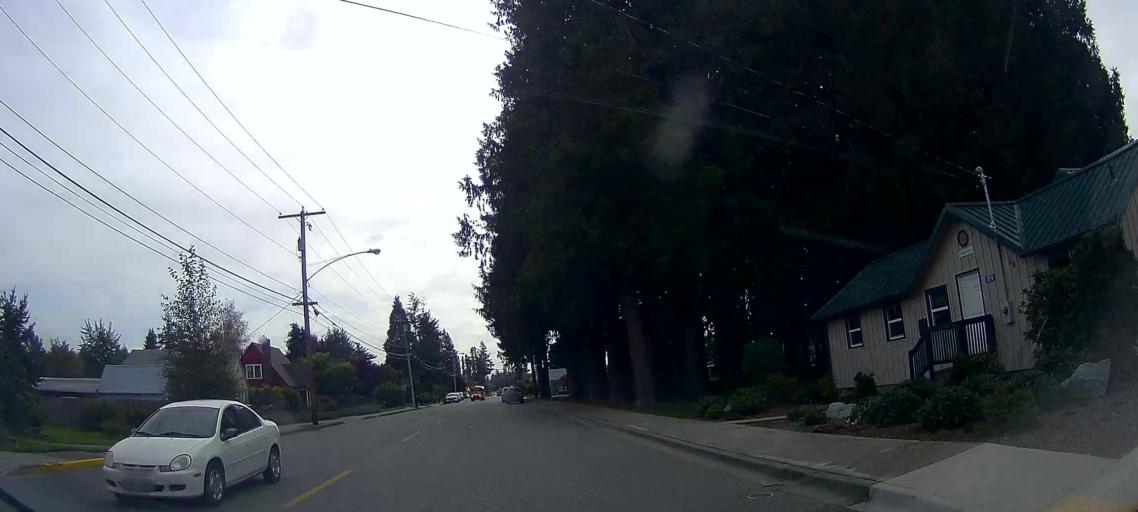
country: US
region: Washington
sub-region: Skagit County
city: Burlington
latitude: 48.4742
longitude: -122.3193
